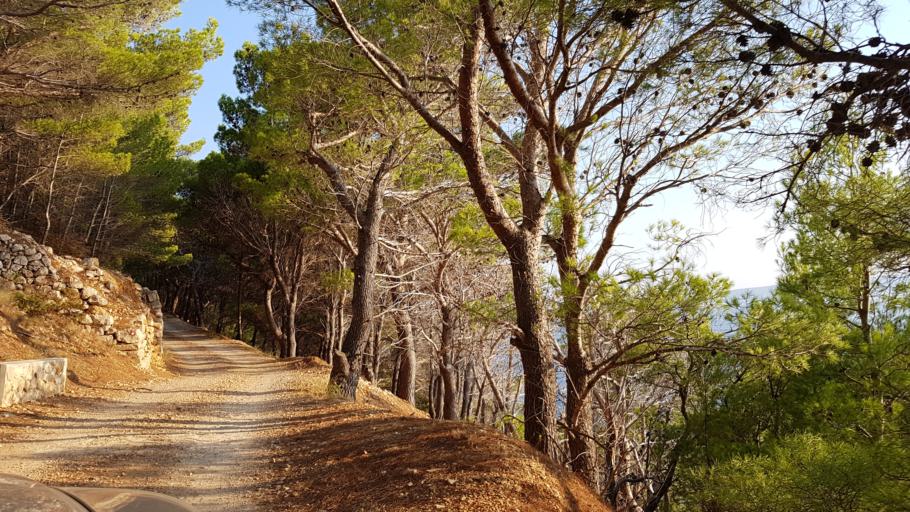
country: HR
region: Splitsko-Dalmatinska
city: Donja Brela
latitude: 43.3889
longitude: 16.8972
